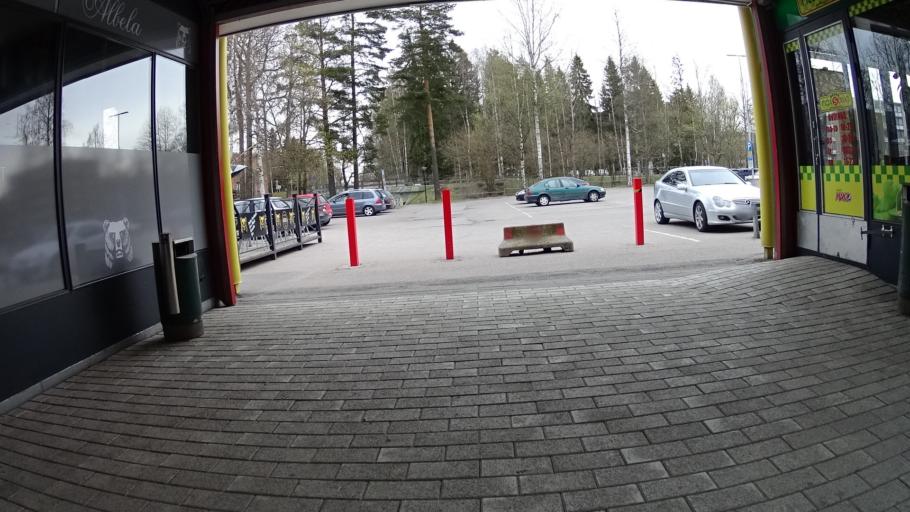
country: FI
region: Uusimaa
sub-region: Helsinki
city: Kilo
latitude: 60.2622
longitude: 24.8046
